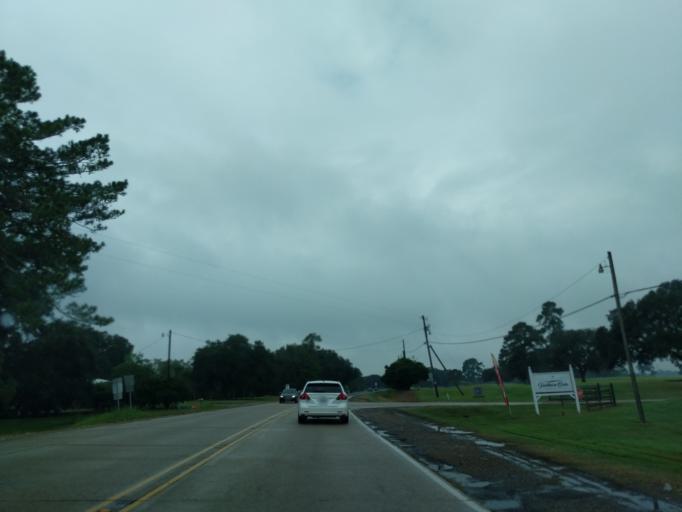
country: US
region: Louisiana
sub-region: Vermilion Parish
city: Abbeville
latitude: 29.9853
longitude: -92.1567
